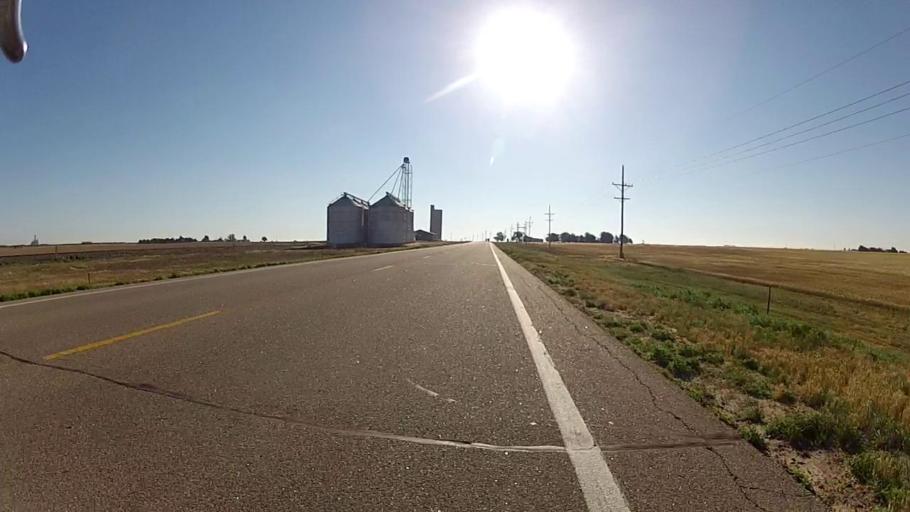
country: US
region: Kansas
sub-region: Haskell County
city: Sublette
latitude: 37.5146
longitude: -100.7312
